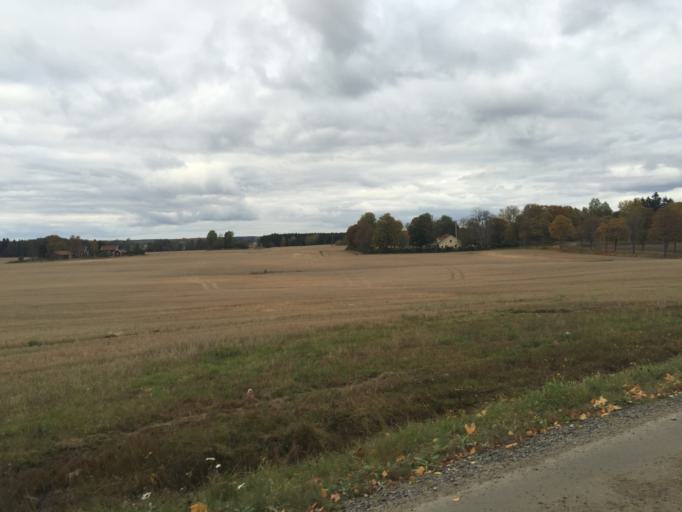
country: SE
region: OErebro
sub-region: Hallsbergs Kommun
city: Palsboda
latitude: 58.8962
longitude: 15.4638
